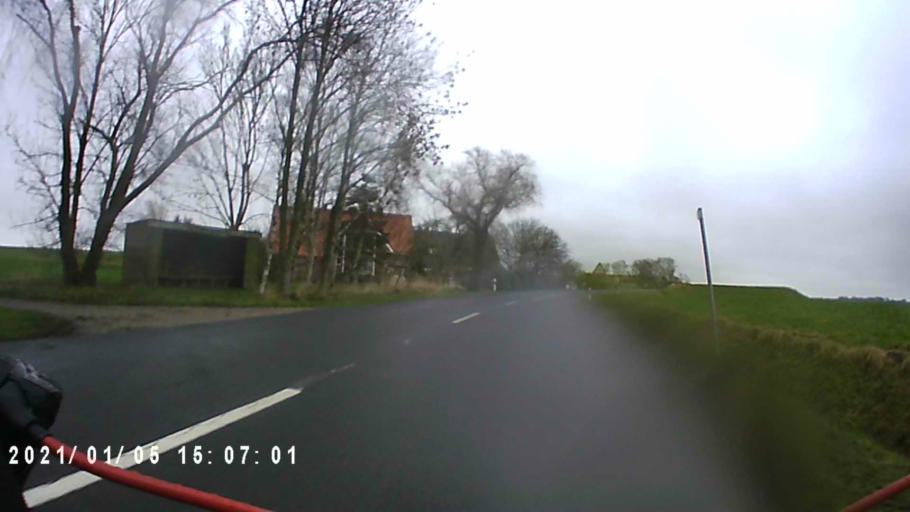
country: DE
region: Lower Saxony
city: Bunde
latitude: 53.2266
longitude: 7.2147
